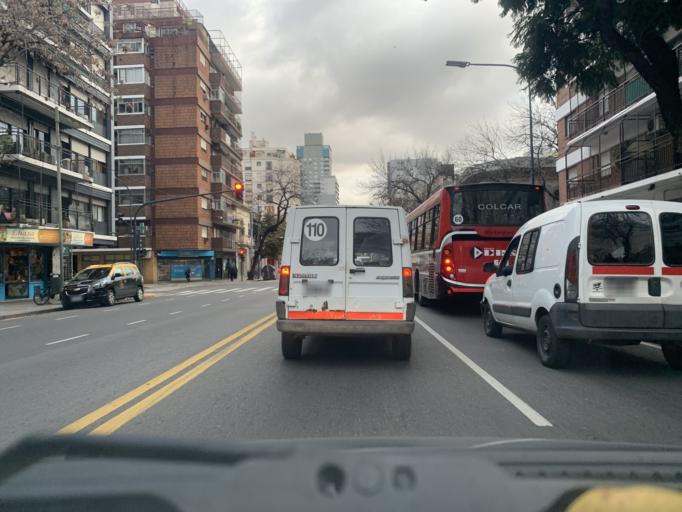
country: AR
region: Buenos Aires F.D.
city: Colegiales
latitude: -34.5795
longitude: -58.4504
